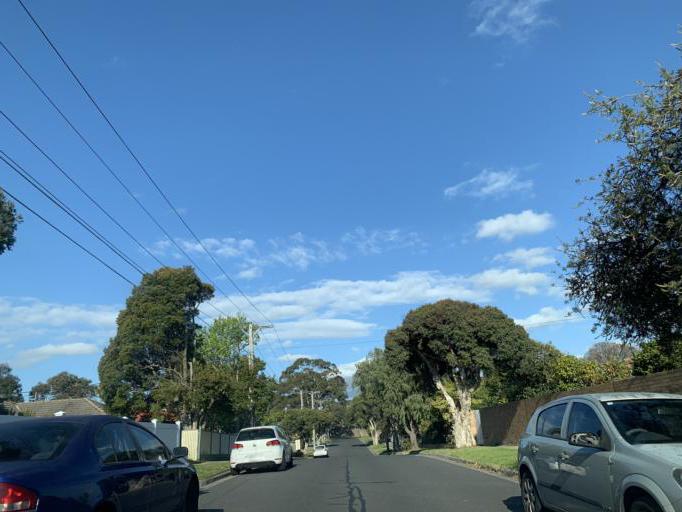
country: AU
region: Victoria
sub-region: Kingston
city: Mordialloc
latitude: -37.9950
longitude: 145.0947
